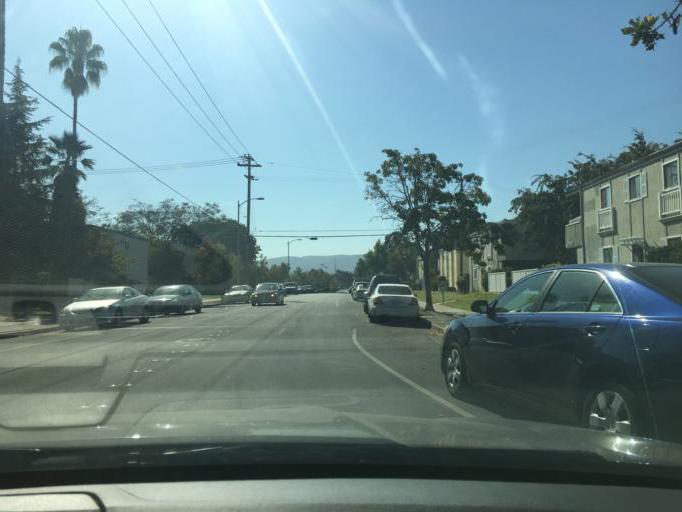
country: US
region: California
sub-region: Santa Clara County
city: Cupertino
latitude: 37.3266
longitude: -122.0368
